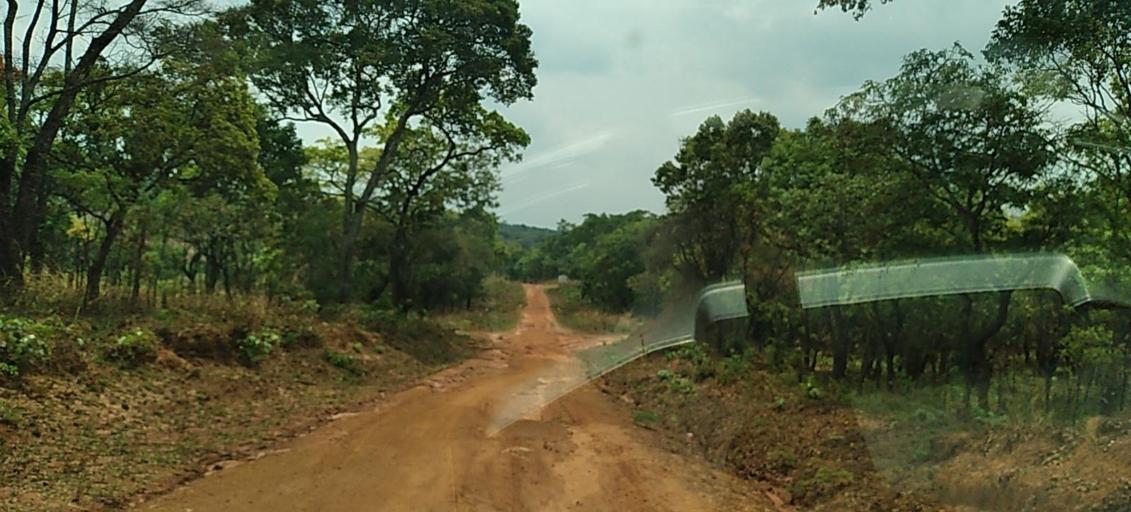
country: ZM
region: North-Western
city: Mwinilunga
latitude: -11.5391
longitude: 24.7820
